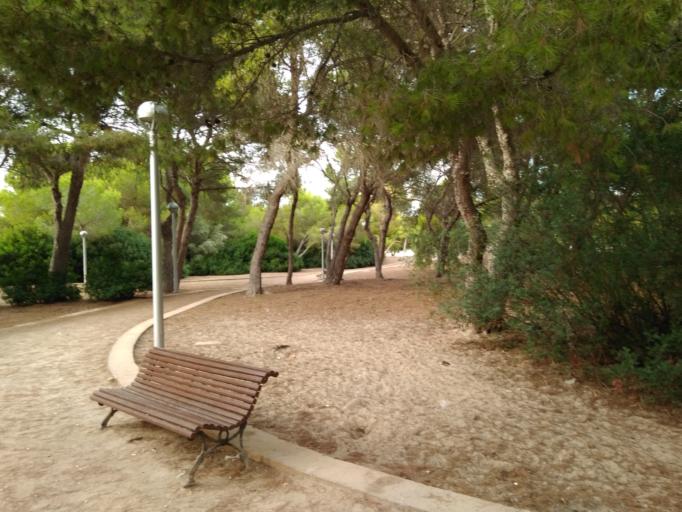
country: ES
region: Balearic Islands
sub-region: Illes Balears
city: s'Arenal
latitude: 39.5294
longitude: 2.7326
